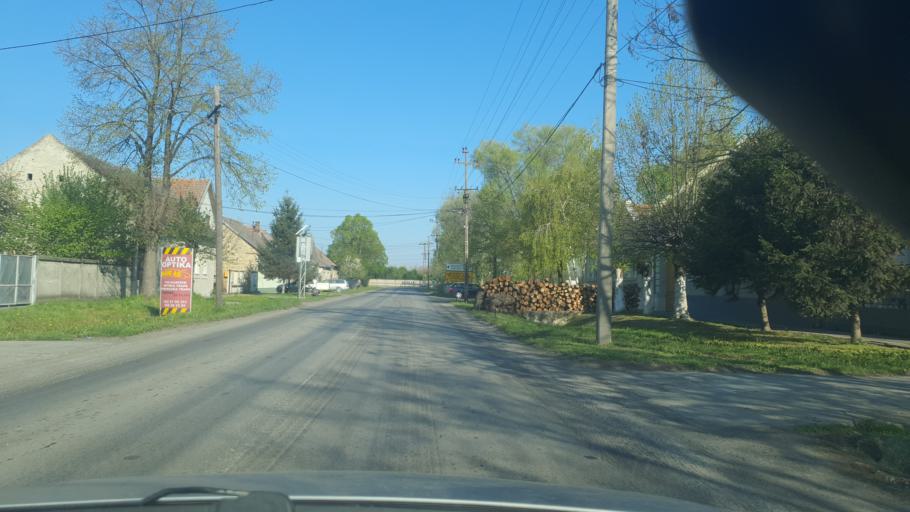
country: RS
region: Autonomna Pokrajina Vojvodina
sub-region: Juznobacki Okrug
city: Vrbas
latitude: 45.5744
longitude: 19.6264
